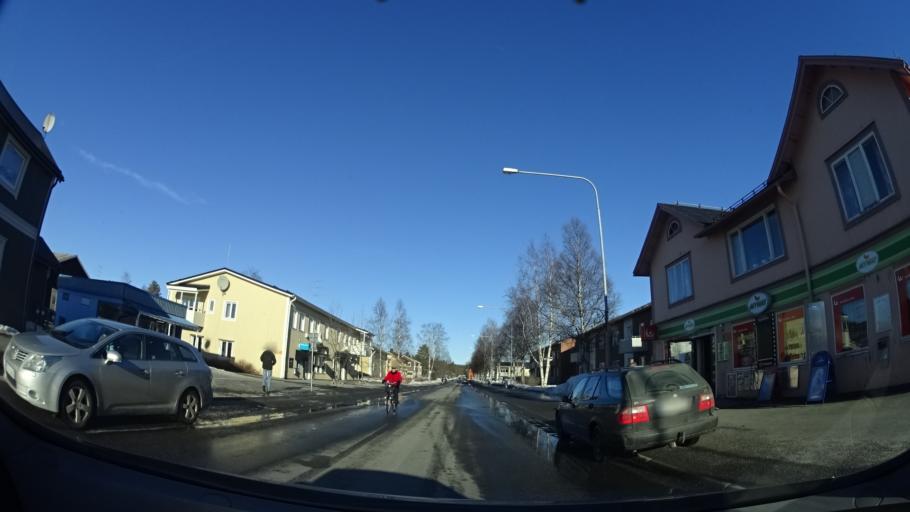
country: SE
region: Vaesterbotten
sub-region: Skelleftea Kommun
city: Byske
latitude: 64.9547
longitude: 21.2046
